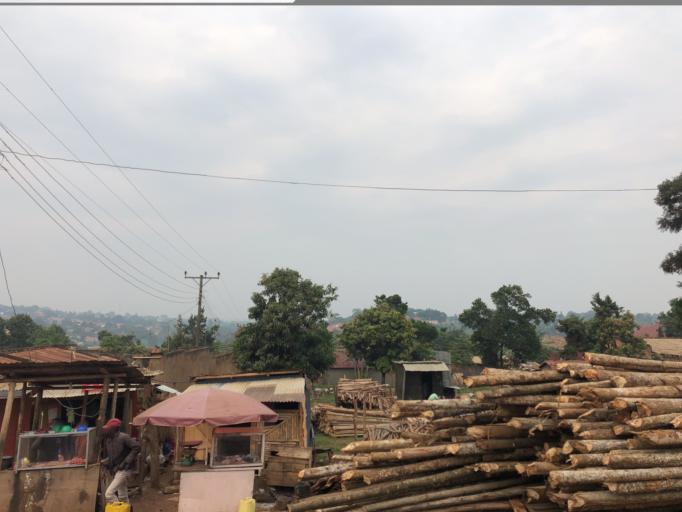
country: UG
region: Central Region
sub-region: Mukono District
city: Mukono
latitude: 0.3641
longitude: 32.7541
